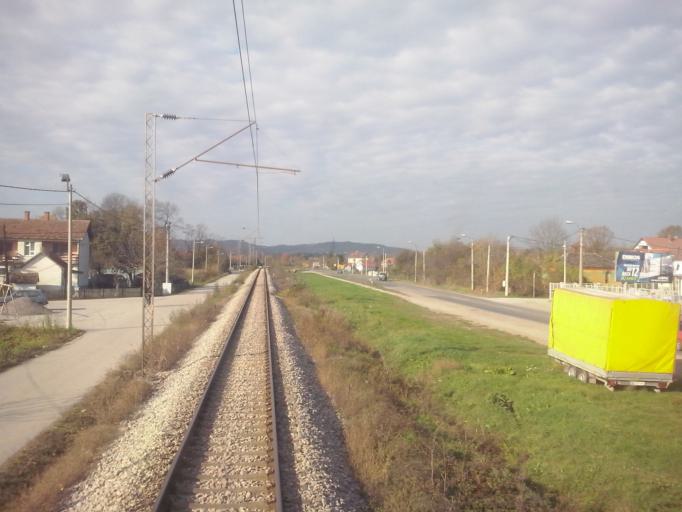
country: RS
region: Central Serbia
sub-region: Kolubarski Okrug
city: Lajkovac
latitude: 44.3646
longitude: 20.1442
